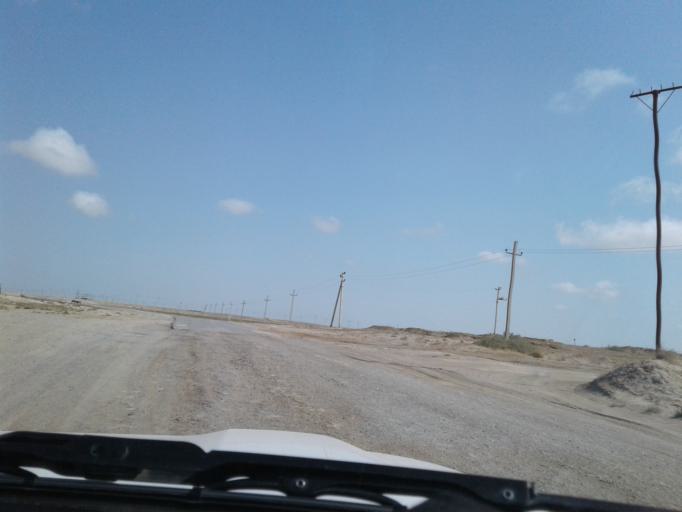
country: IR
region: Golestan
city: Gomishan
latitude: 37.7133
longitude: 53.9412
